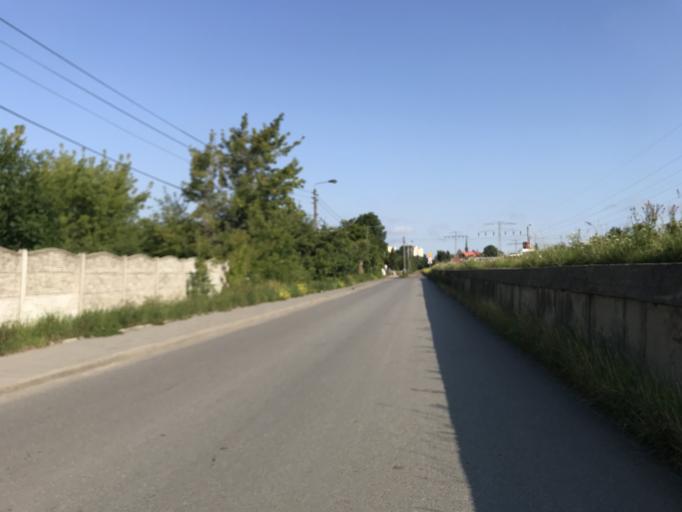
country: PL
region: Pomeranian Voivodeship
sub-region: Gdansk
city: Gdansk
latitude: 54.3450
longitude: 18.6807
